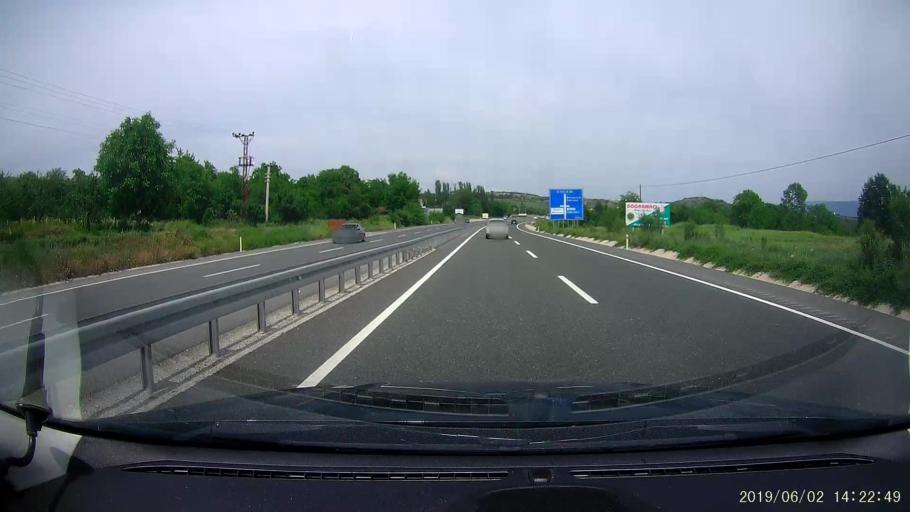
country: TR
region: Kastamonu
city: Tosya
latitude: 40.9988
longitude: 34.0235
